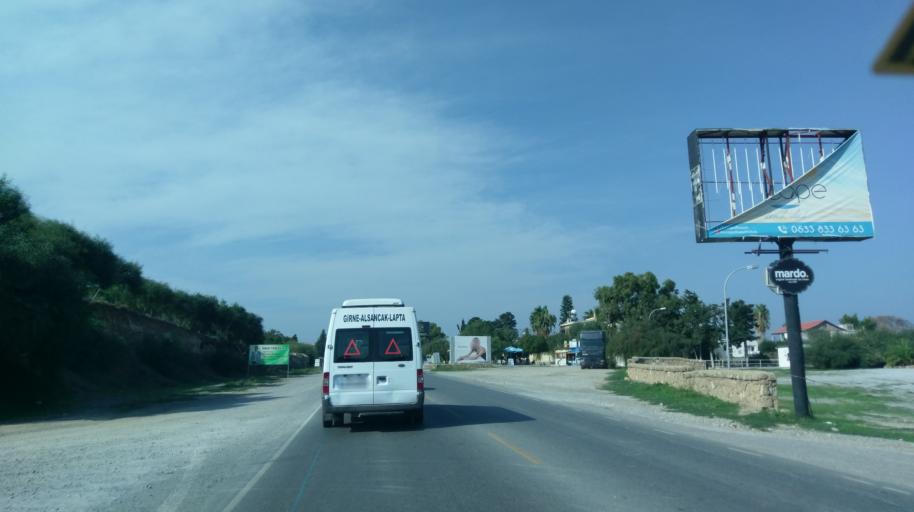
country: CY
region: Keryneia
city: Lapithos
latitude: 35.3454
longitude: 33.2341
